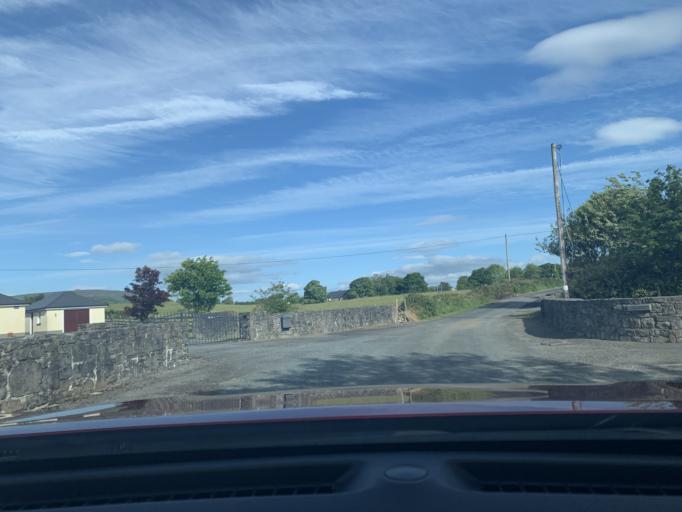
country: IE
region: Connaught
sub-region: Sligo
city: Sligo
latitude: 54.2533
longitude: -8.5042
